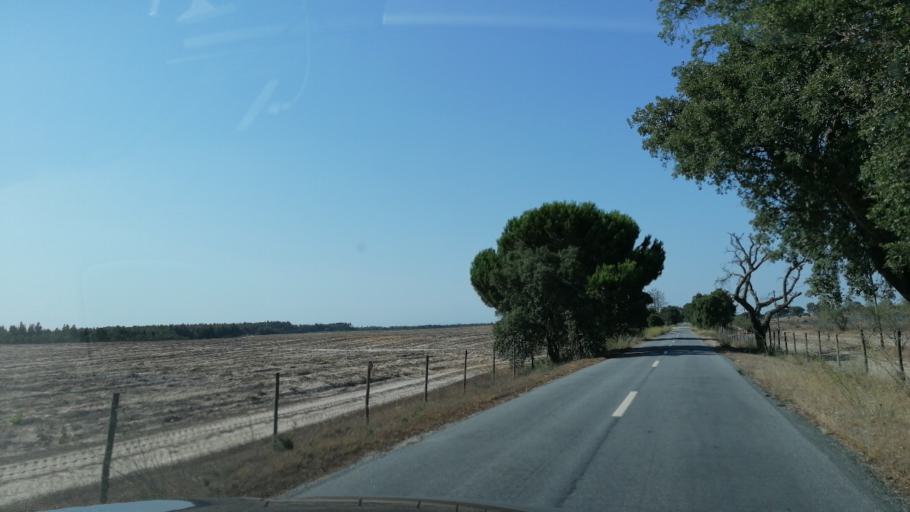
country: PT
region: Evora
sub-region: Vendas Novas
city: Vendas Novas
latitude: 38.7247
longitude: -8.6208
